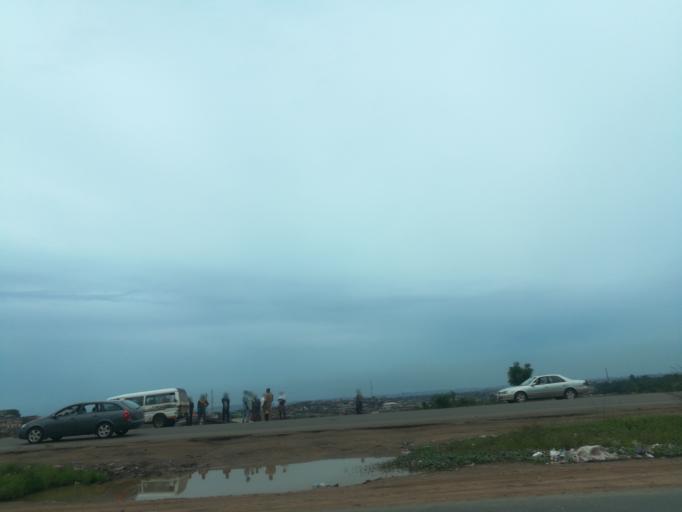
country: NG
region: Oyo
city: Ibadan
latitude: 7.3495
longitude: 3.9195
